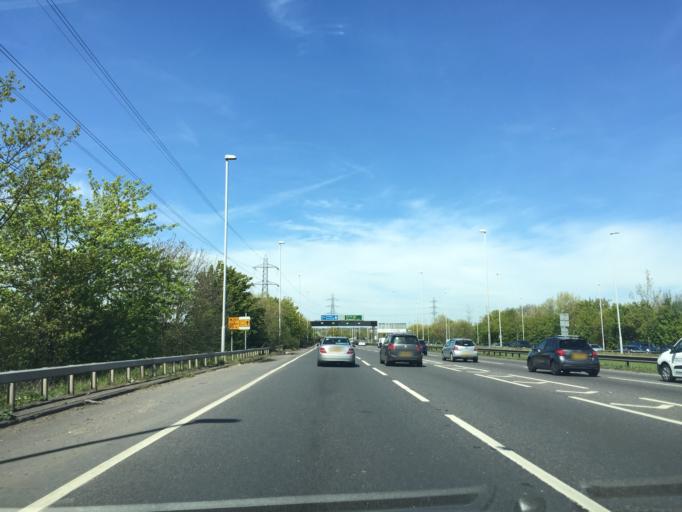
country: GB
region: England
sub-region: Greater London
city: Woodford Green
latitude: 51.5787
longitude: 0.0419
